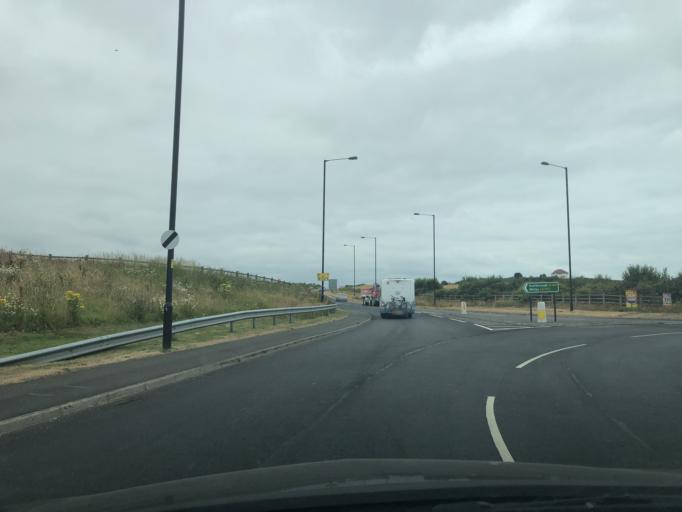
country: GB
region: England
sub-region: North Yorkshire
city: Scarborough
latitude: 54.2419
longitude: -0.3664
